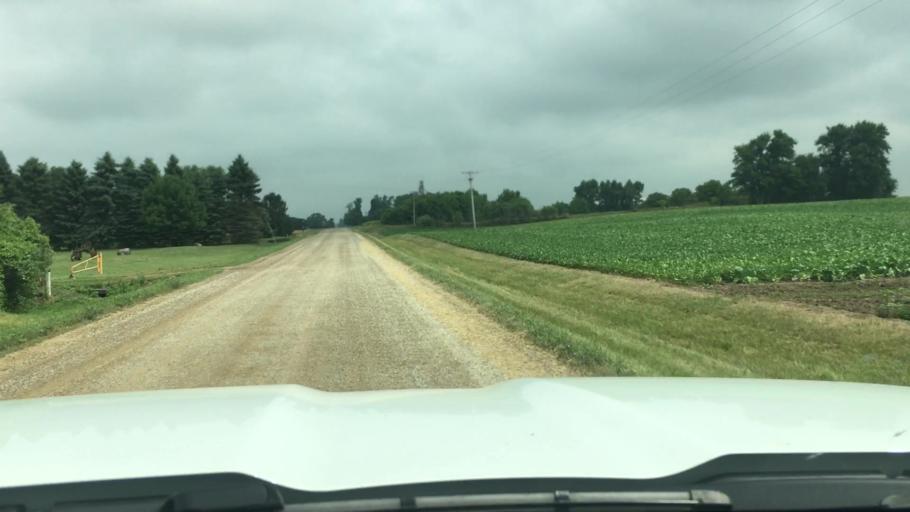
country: US
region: Michigan
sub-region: Sanilac County
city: Marlette
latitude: 43.3407
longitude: -82.9750
